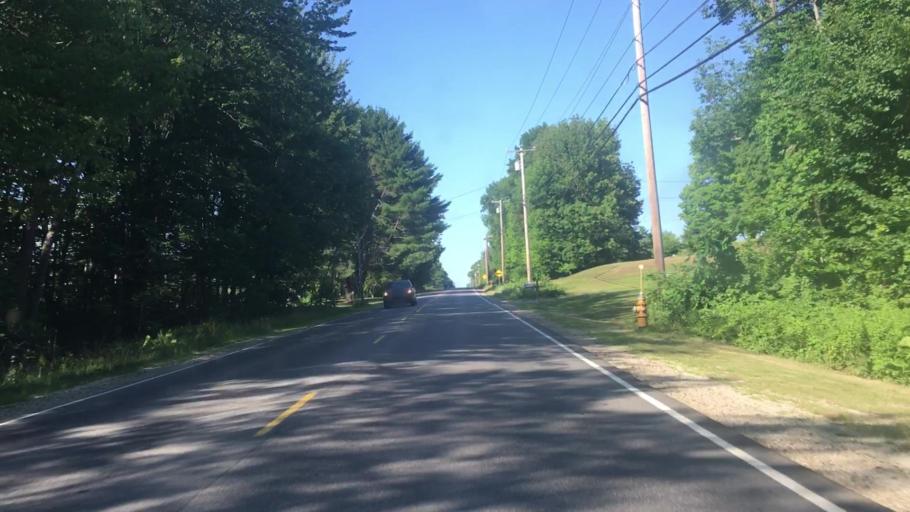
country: US
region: Maine
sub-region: York County
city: Buxton
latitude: 43.7429
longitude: -70.5435
